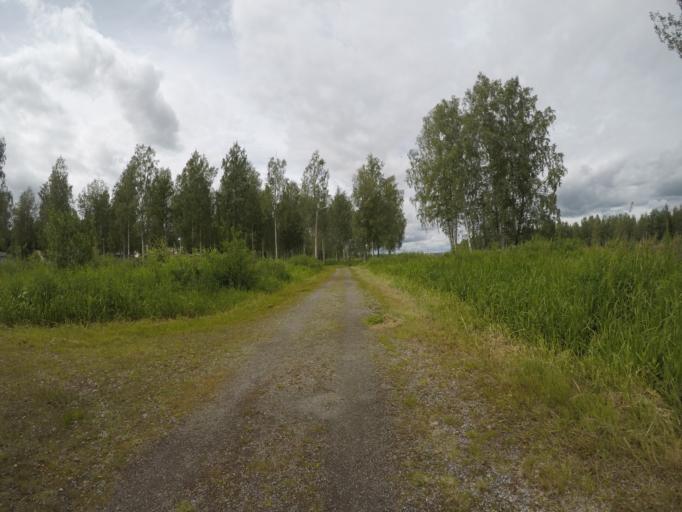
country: FI
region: Haeme
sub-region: Haemeenlinna
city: Haemeenlinna
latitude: 60.9830
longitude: 24.4820
